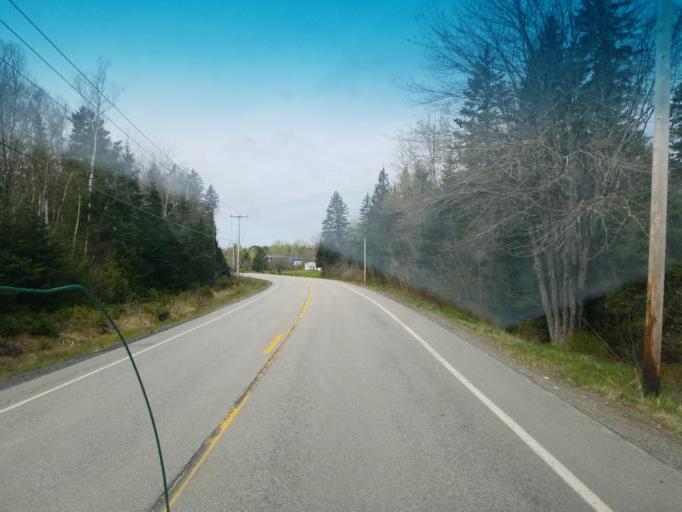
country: US
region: Maine
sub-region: Washington County
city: Eastport
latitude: 44.8015
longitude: -67.1352
